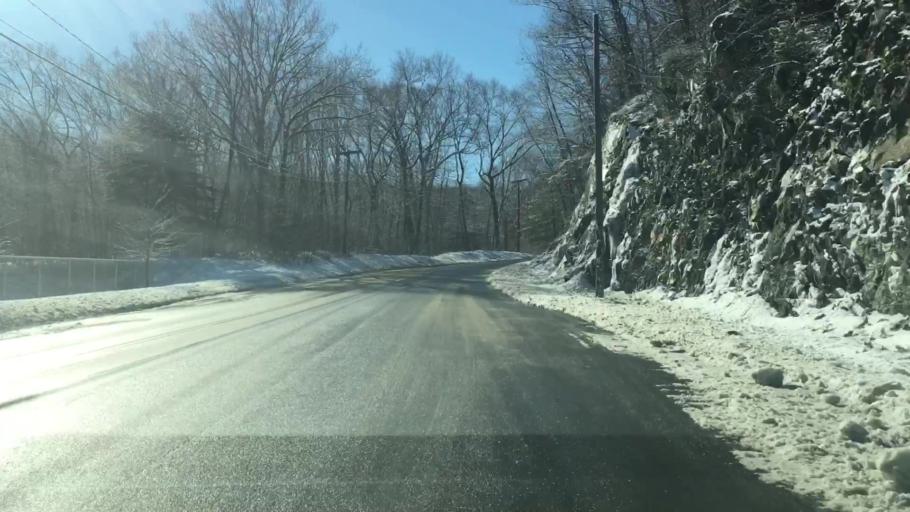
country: US
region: Connecticut
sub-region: Litchfield County
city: Oakville
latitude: 41.6116
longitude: -73.0645
